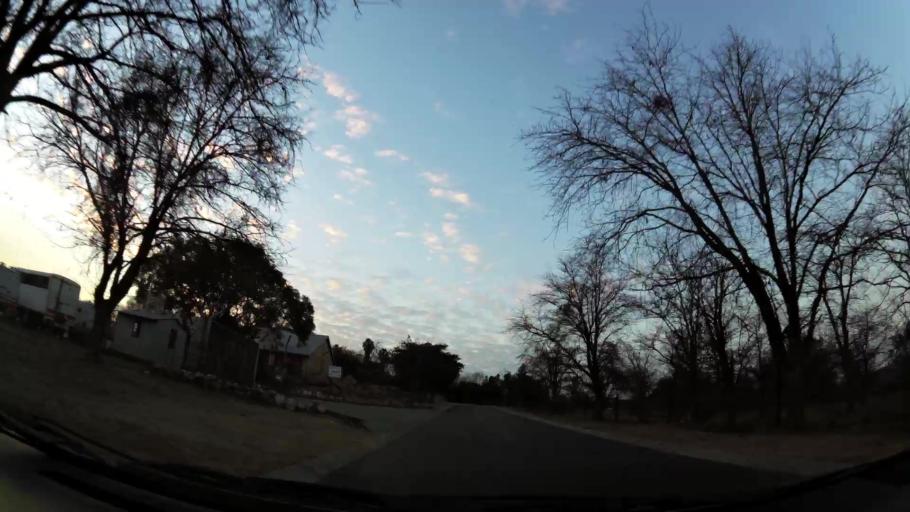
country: ZA
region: Gauteng
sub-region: City of Johannesburg Metropolitan Municipality
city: Diepsloot
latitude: -26.0054
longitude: 28.0486
